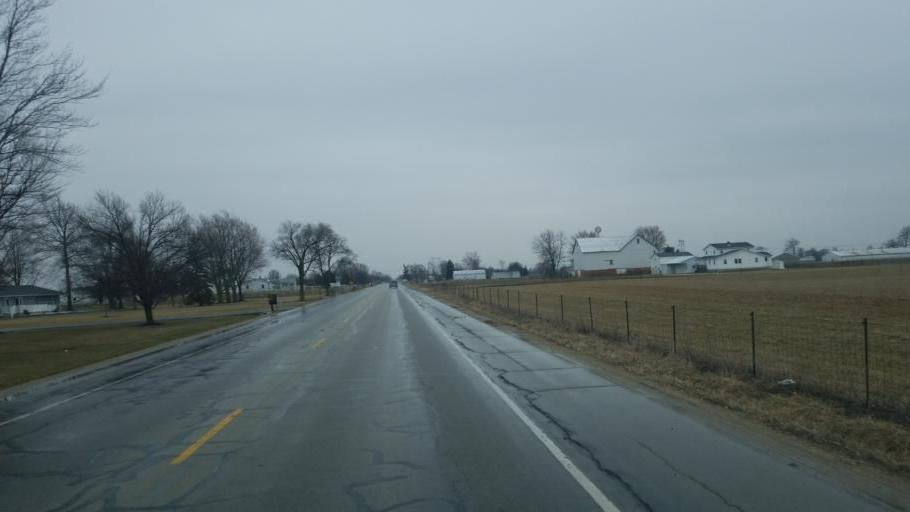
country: US
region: Indiana
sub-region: Adams County
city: Berne
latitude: 40.7120
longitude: -84.9559
